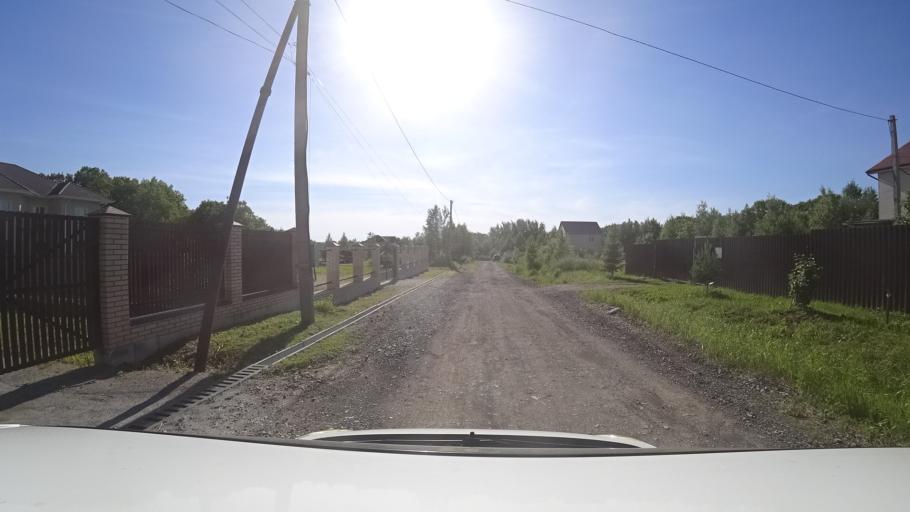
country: RU
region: Khabarovsk Krai
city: Topolevo
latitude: 48.5440
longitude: 135.1704
